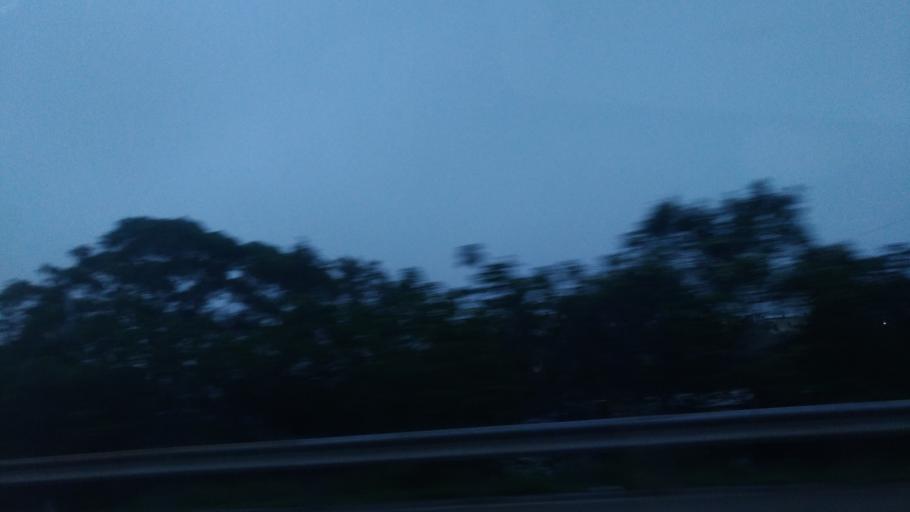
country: TW
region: Taiwan
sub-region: Hsinchu
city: Hsinchu
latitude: 24.7382
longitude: 120.9162
